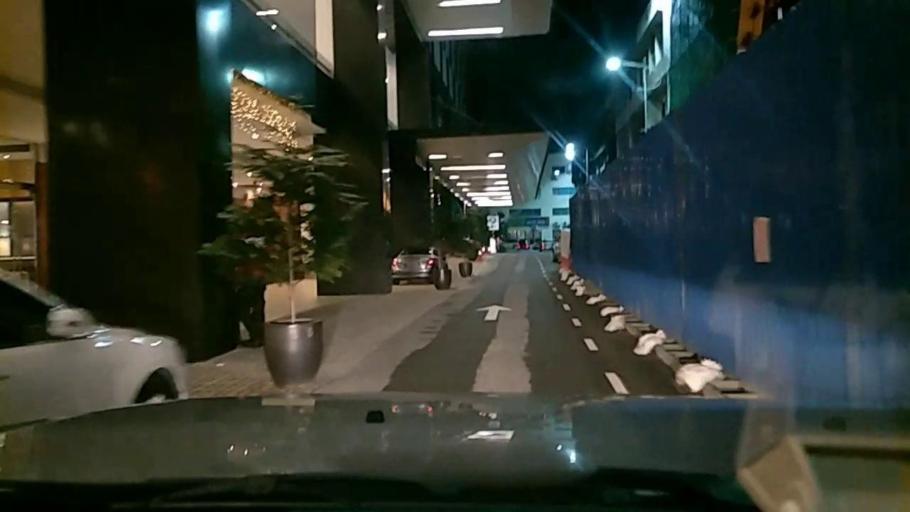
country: MY
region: Selangor
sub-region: Petaling
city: Petaling Jaya
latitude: 3.1269
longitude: 101.6168
